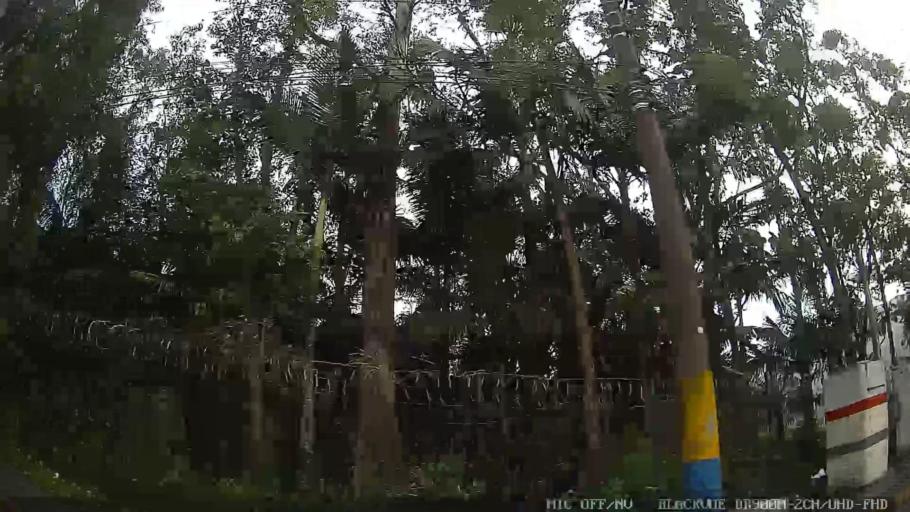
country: BR
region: Sao Paulo
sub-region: Cubatao
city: Cubatao
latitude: -23.8741
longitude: -46.4277
